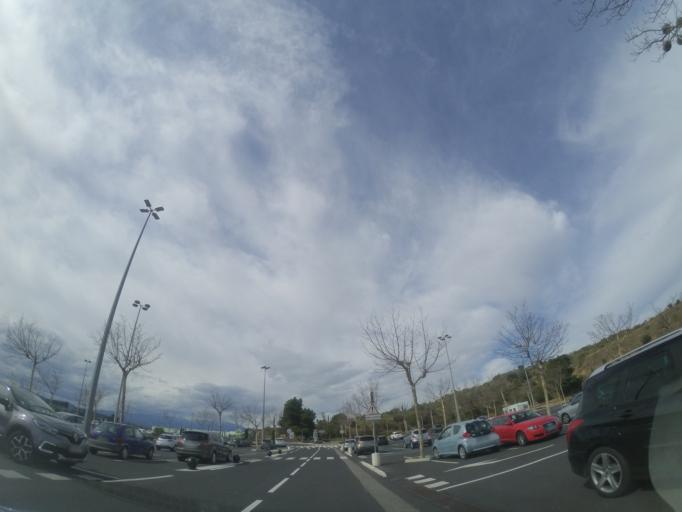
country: FR
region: Languedoc-Roussillon
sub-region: Departement des Pyrenees-Orientales
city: Pollestres
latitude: 42.6702
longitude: 2.8800
